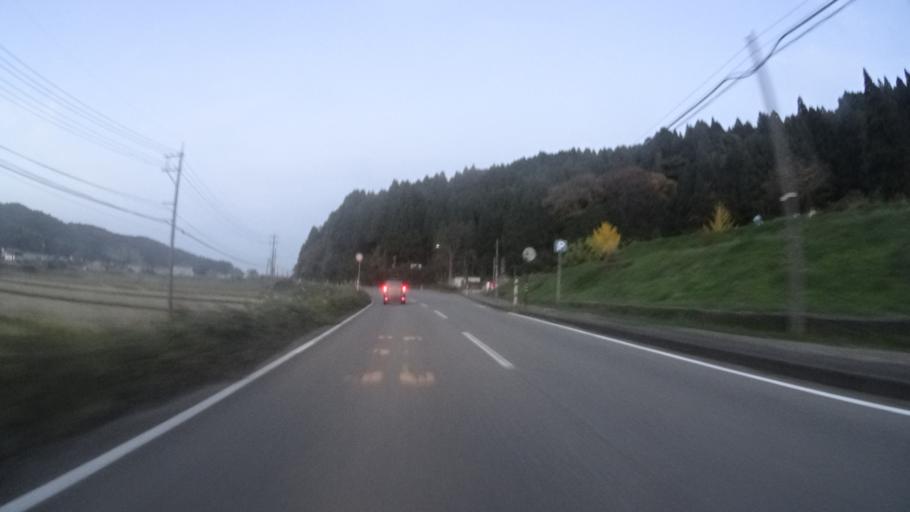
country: JP
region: Ishikawa
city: Nanao
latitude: 37.3732
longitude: 136.8785
